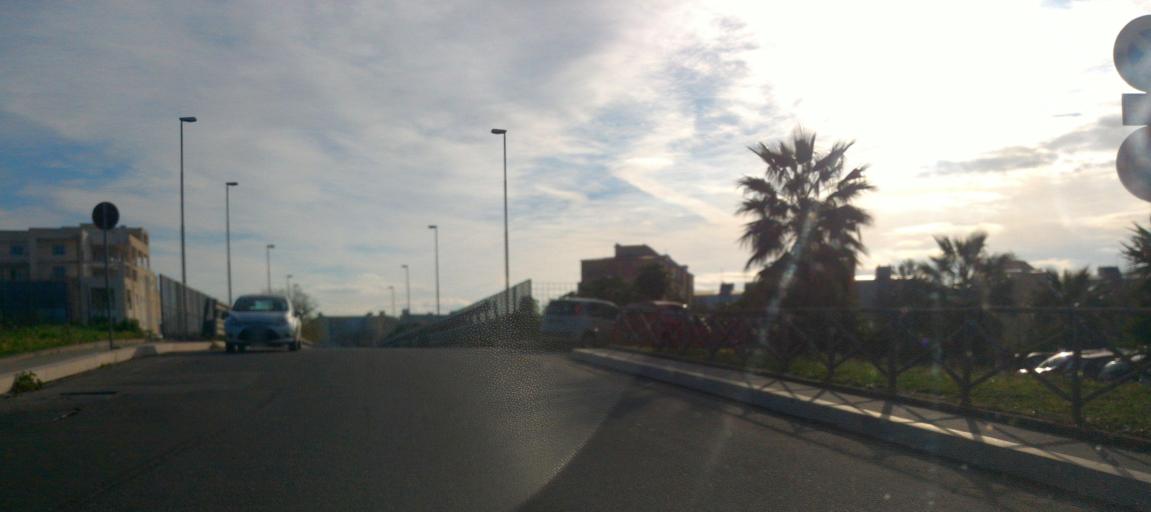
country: IT
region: Calabria
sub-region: Provincia di Crotone
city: Crotone
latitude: 39.0839
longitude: 17.1112
